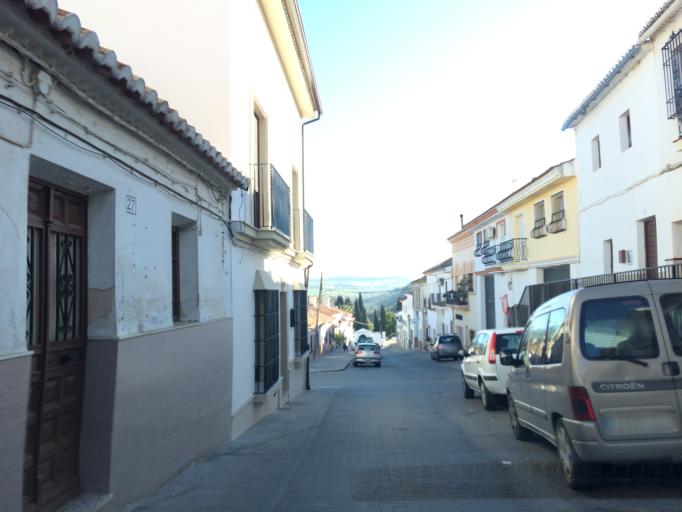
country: ES
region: Andalusia
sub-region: Provincia de Malaga
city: Casabermeja
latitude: 36.8945
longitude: -4.4278
